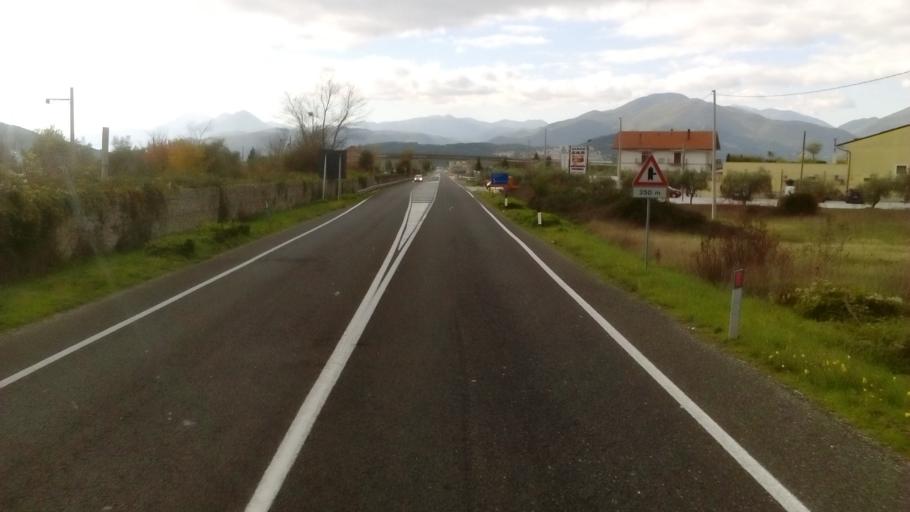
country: IT
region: Molise
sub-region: Provincia di Isernia
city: Macchia d'Isernia
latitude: 41.5656
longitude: 14.1999
